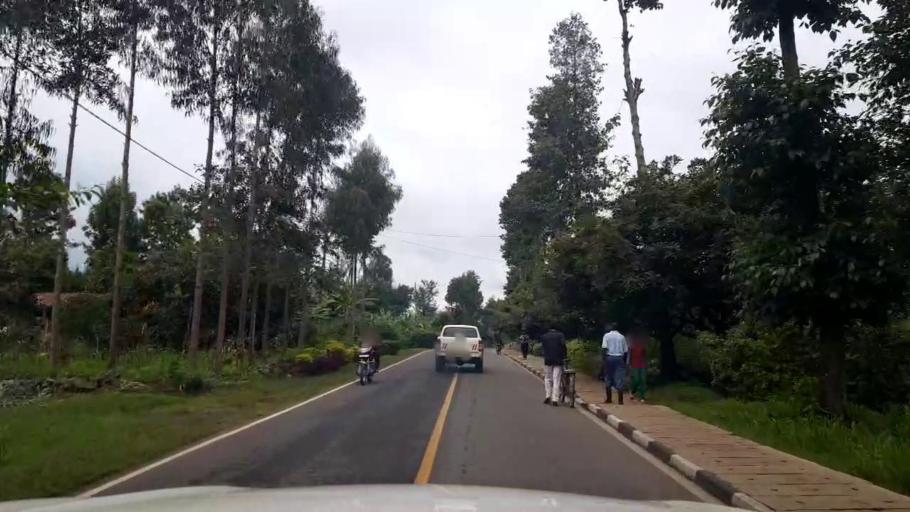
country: RW
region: Northern Province
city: Musanze
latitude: -1.4535
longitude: 29.6008
